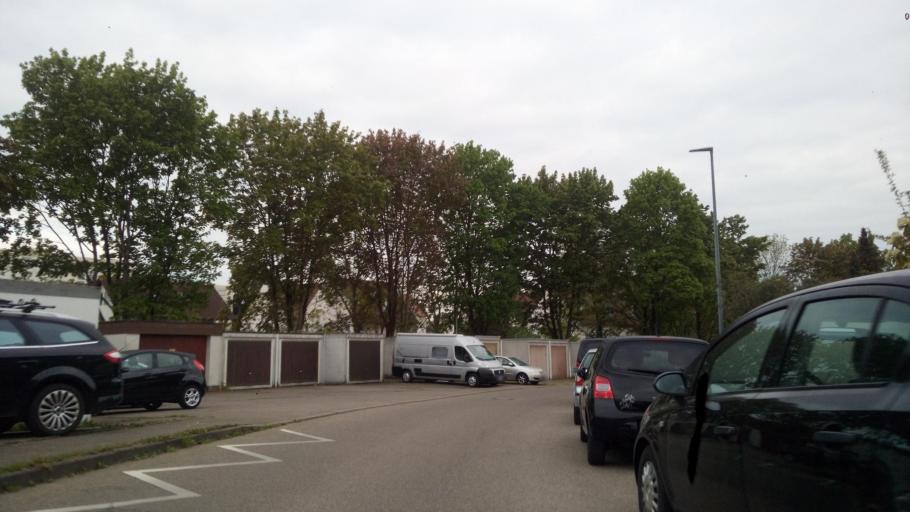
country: DE
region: Baden-Wuerttemberg
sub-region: Regierungsbezirk Stuttgart
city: Eislingen
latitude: 48.7020
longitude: 9.7165
